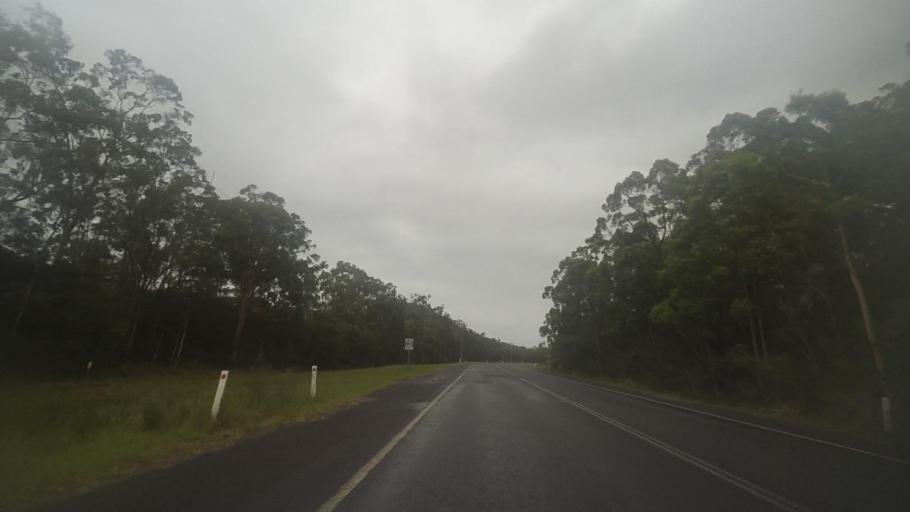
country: AU
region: New South Wales
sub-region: Port Stephens Shire
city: Port Stephens
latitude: -32.6363
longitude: 151.9949
